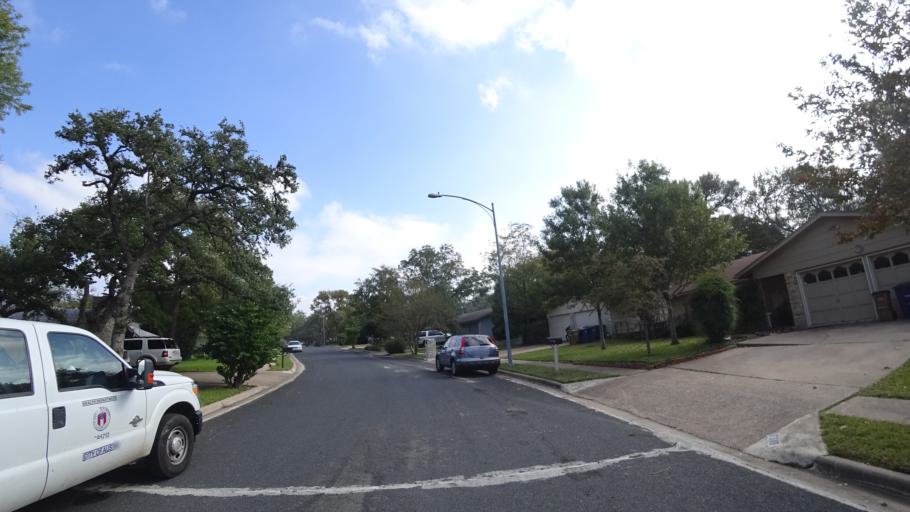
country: US
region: Texas
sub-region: Travis County
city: Shady Hollow
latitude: 30.2021
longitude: -97.8163
